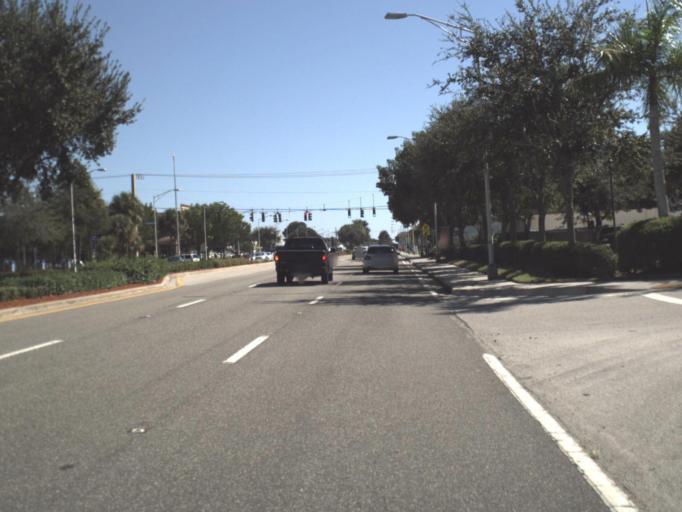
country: US
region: Florida
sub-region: Collier County
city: Naples
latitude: 26.1384
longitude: -81.7720
